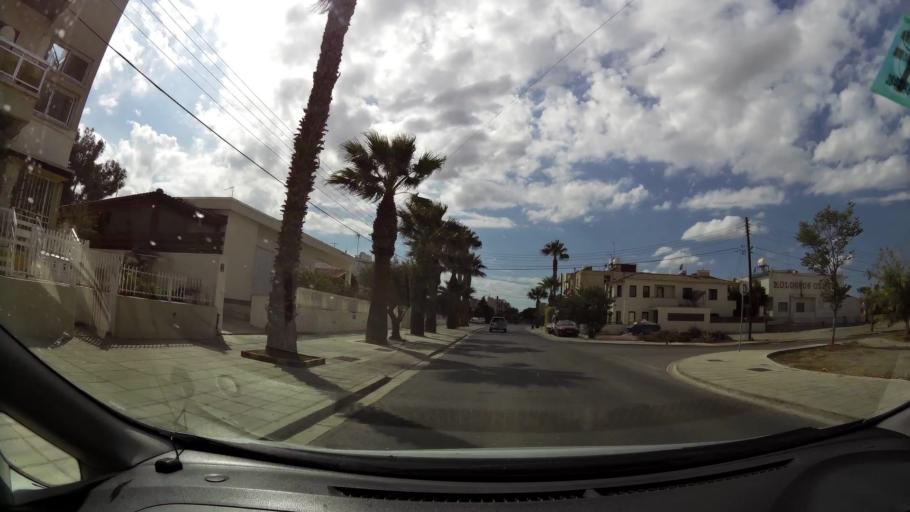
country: CY
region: Lefkosia
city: Nicosia
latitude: 35.1884
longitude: 33.3878
